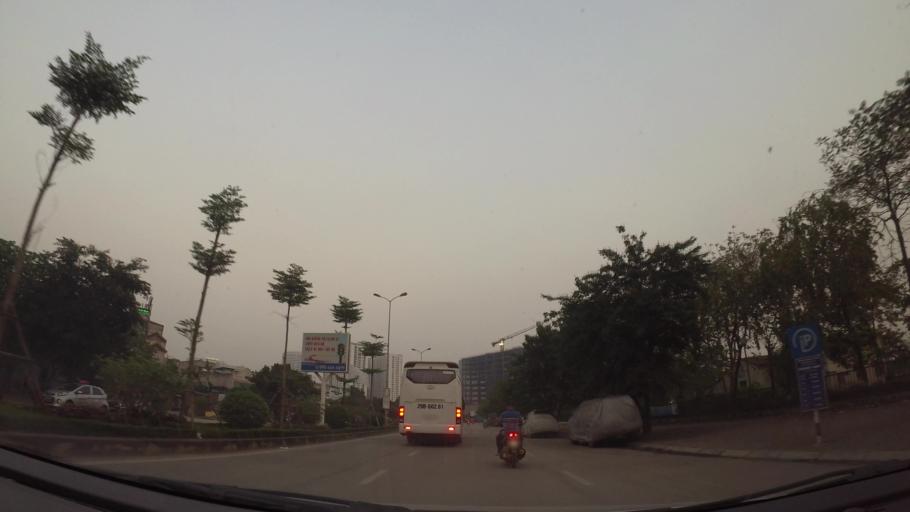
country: VN
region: Ha Noi
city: Tay Ho
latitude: 21.0660
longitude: 105.7887
